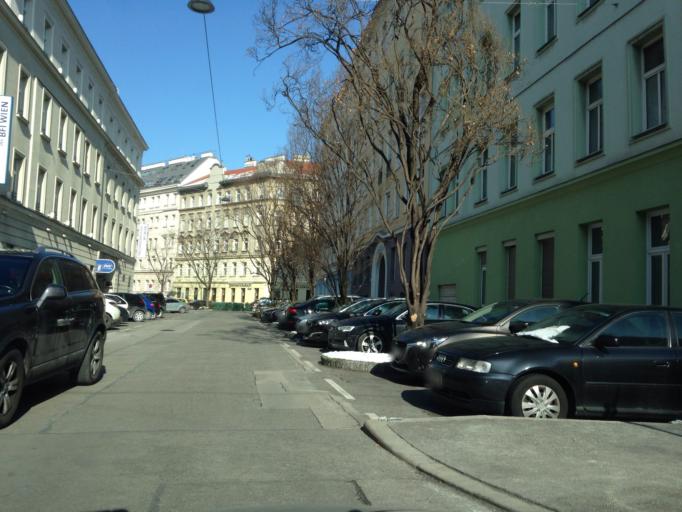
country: AT
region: Vienna
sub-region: Wien Stadt
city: Vienna
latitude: 48.2188
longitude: 16.4036
